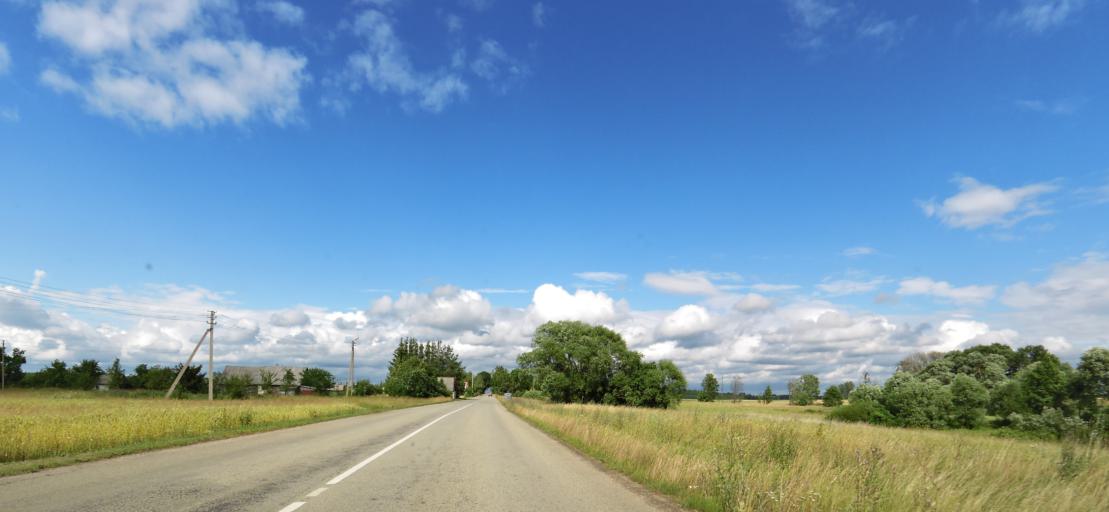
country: LT
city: Kupiskis
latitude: 55.8995
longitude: 25.0203
